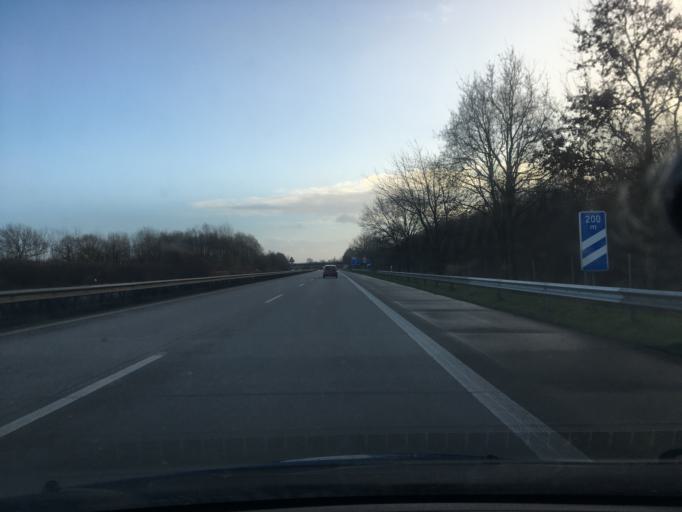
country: DE
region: Schleswig-Holstein
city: Kolln-Reisiek
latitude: 53.7490
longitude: 9.7105
